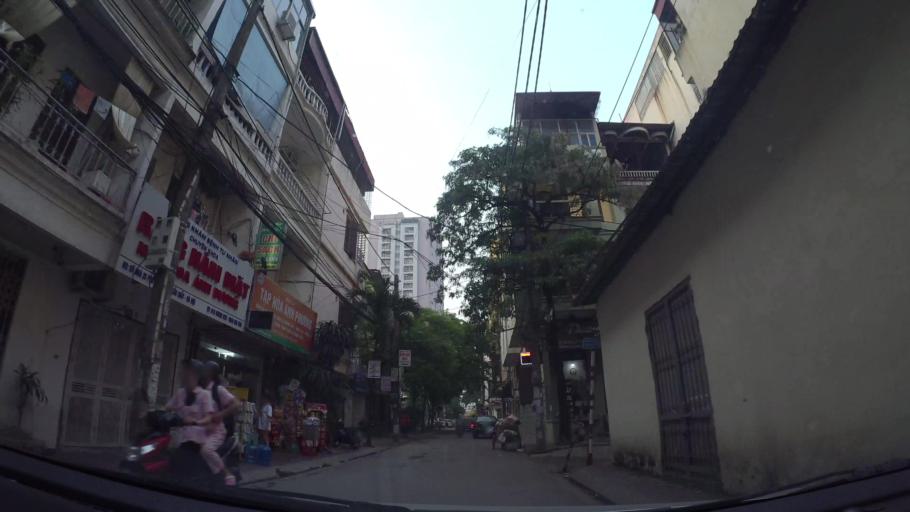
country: VN
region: Ha Noi
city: Cau Giay
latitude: 21.0484
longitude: 105.7959
